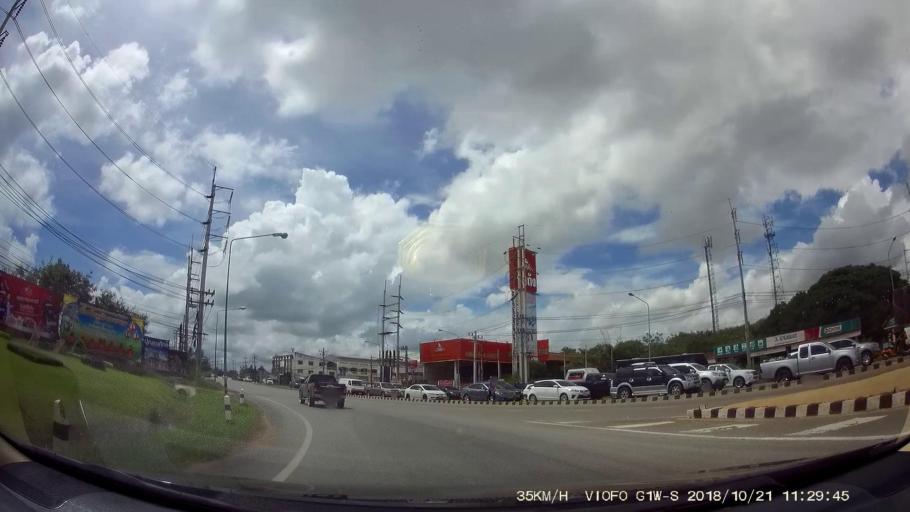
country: TH
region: Chaiyaphum
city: Chaiyaphum
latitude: 15.7859
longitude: 102.0282
